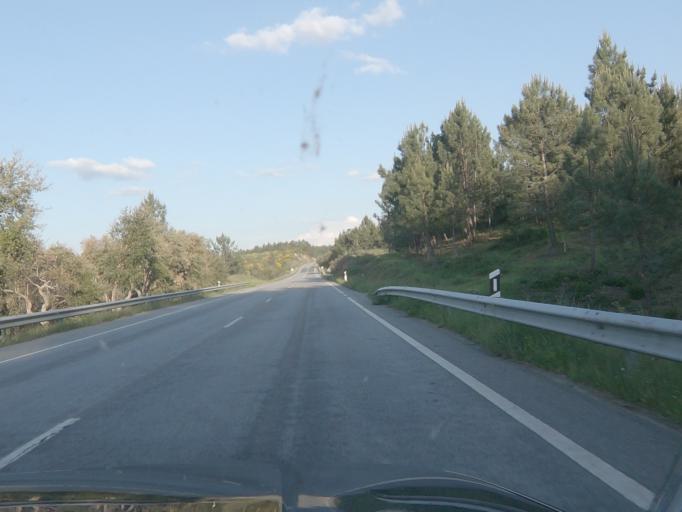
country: PT
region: Portalegre
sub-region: Marvao
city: Marvao
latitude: 39.3730
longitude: -7.3542
